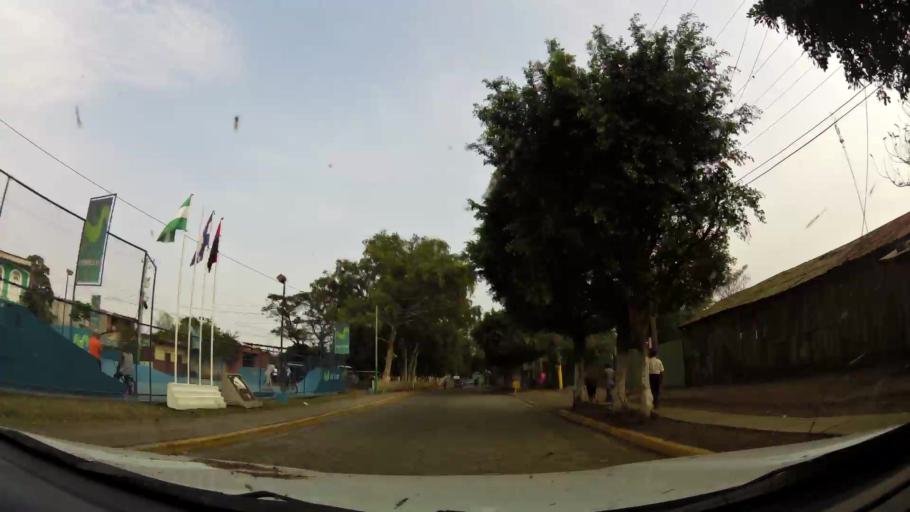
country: NI
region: Masaya
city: Masaya
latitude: 11.9831
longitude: -86.0979
